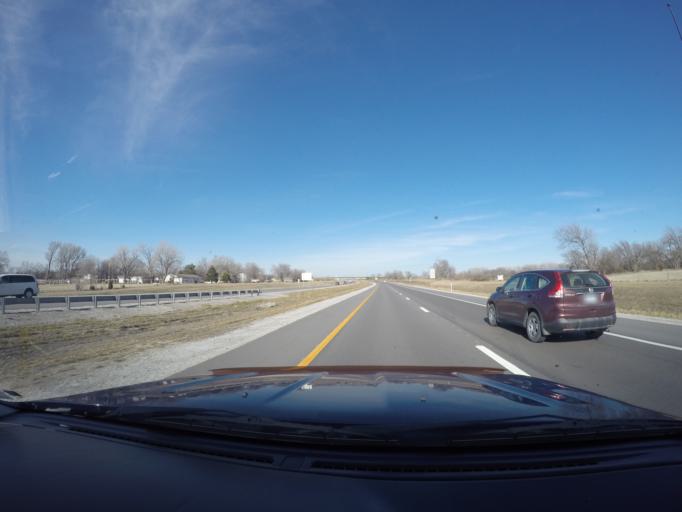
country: US
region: Kansas
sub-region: Sedgwick County
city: Park City
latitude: 37.8062
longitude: -97.3269
